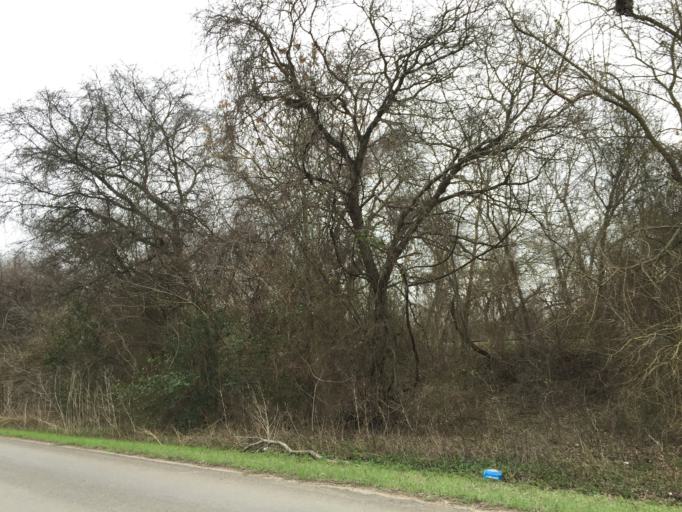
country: US
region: Texas
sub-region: Bell County
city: Belton
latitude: 31.0455
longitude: -97.4202
